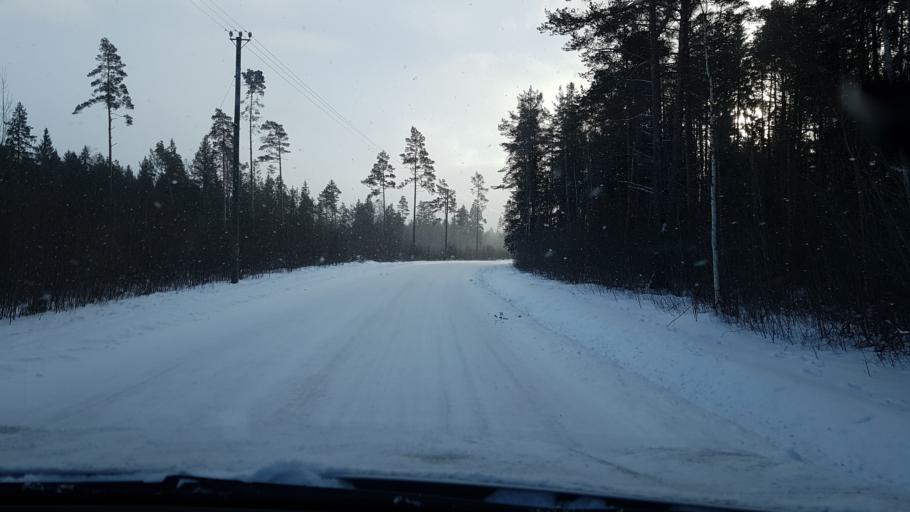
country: EE
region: Harju
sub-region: Nissi vald
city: Turba
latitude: 59.1947
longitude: 24.1399
